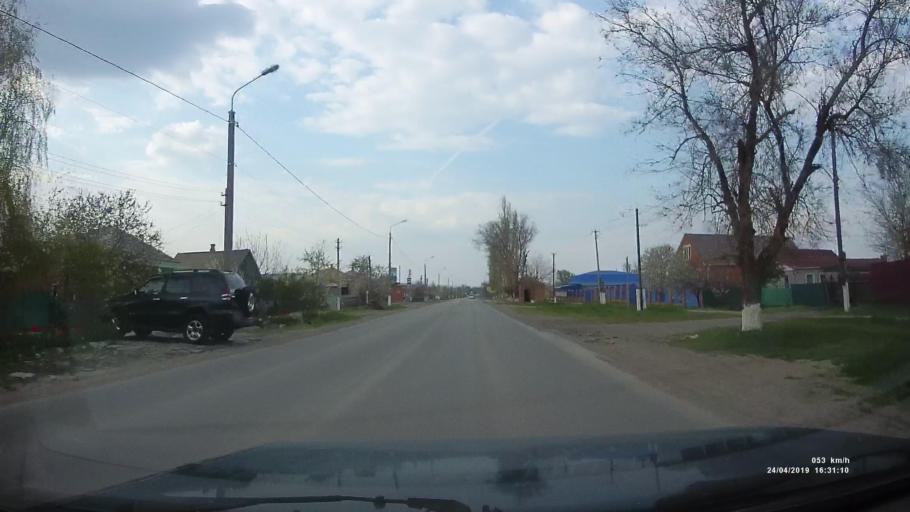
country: RU
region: Rostov
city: Orlovskiy
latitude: 46.8790
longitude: 42.0384
